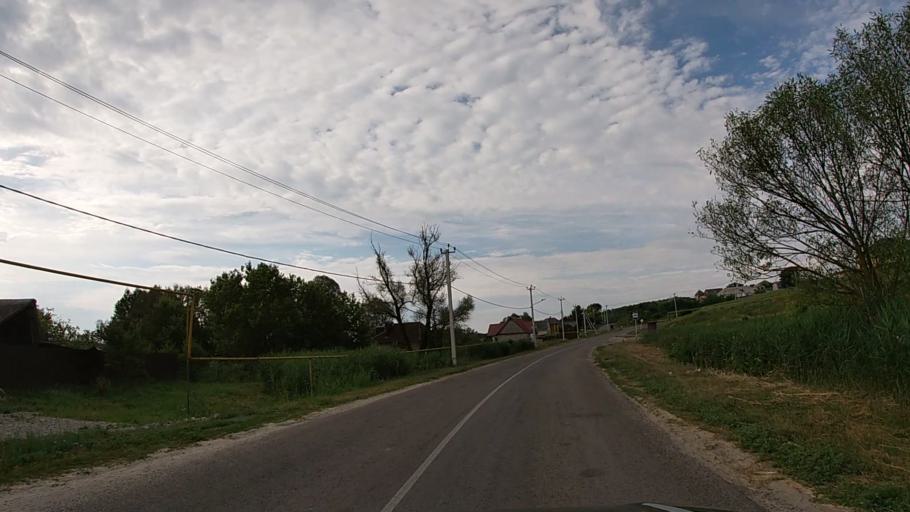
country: RU
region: Belgorod
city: Severnyy
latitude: 50.7079
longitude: 36.6005
